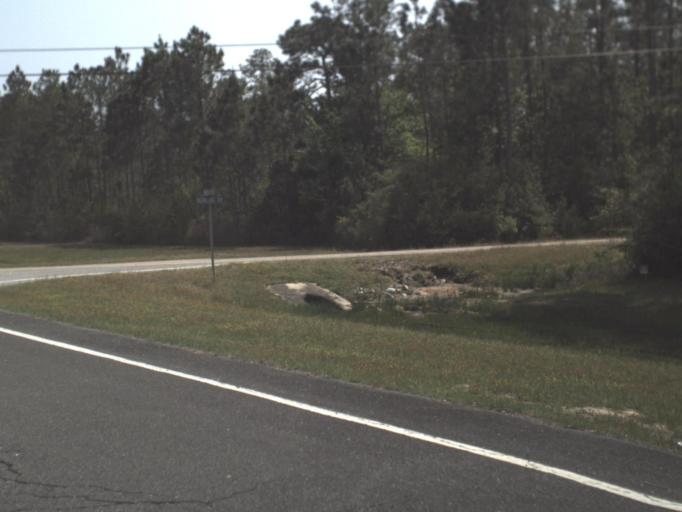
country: US
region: Florida
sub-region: Santa Rosa County
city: Bagdad
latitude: 30.5087
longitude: -87.0821
